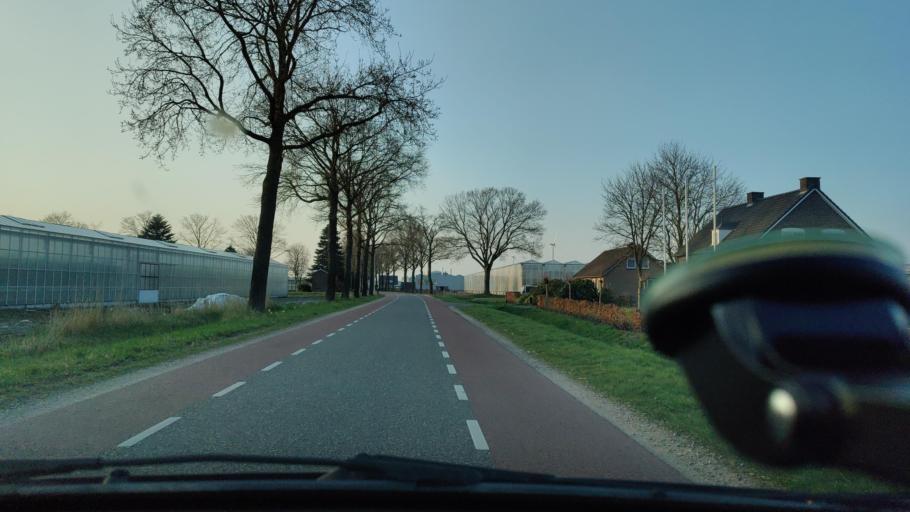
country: NL
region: Limburg
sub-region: Gemeente Bergen
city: Wellerlooi
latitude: 51.5411
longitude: 6.1710
